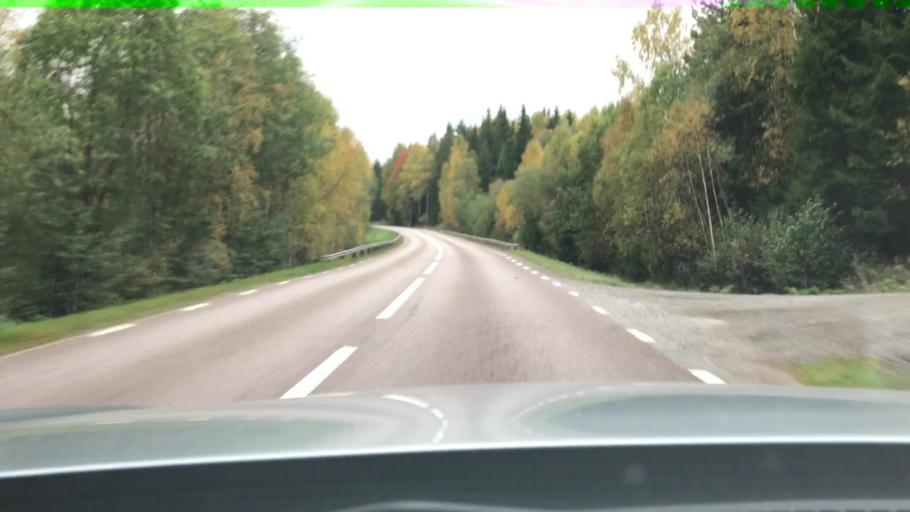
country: SE
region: Vaermland
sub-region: Eda Kommun
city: Amotfors
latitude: 59.7351
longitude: 12.2167
